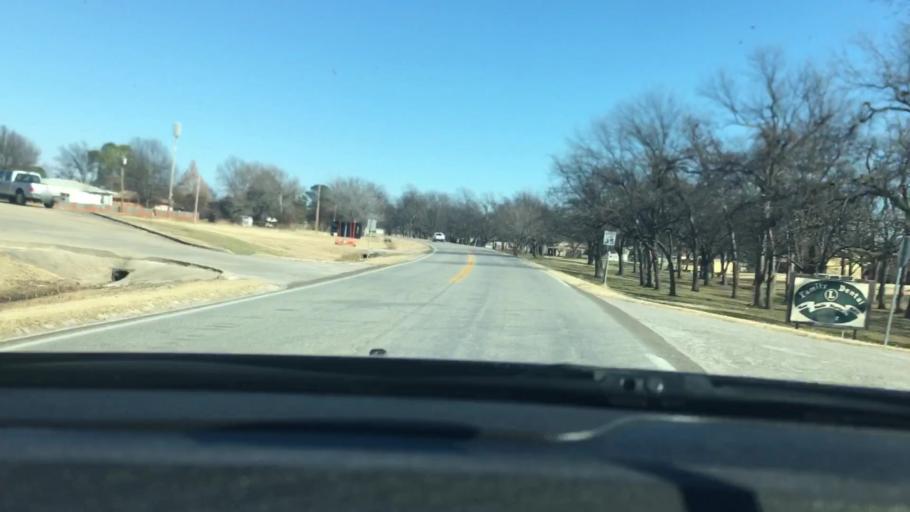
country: US
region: Oklahoma
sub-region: Garvin County
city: Wynnewood
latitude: 34.6451
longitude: -97.1556
